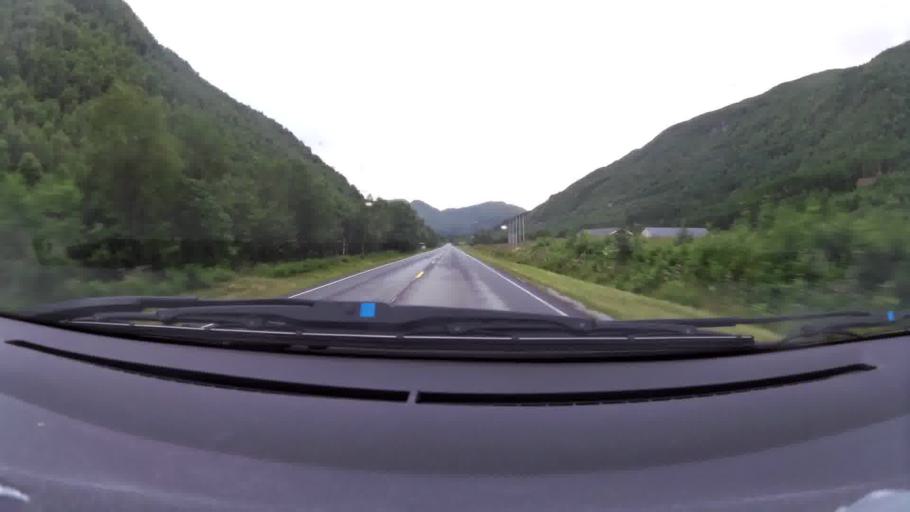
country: NO
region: More og Romsdal
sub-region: Molde
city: Molde
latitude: 62.7971
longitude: 7.2931
